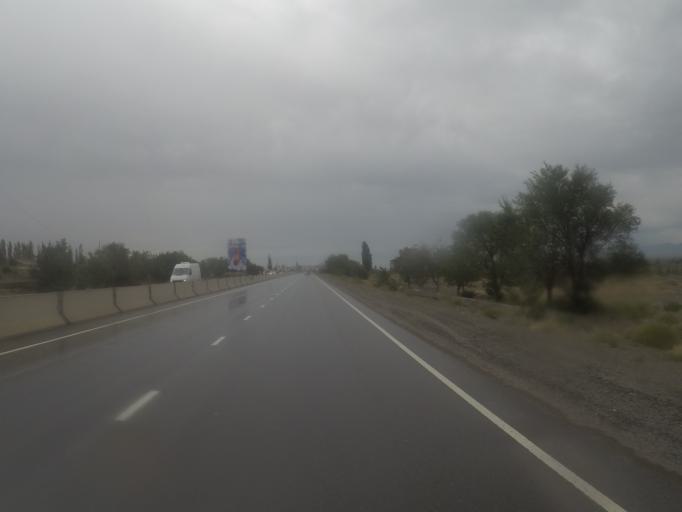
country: KG
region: Ysyk-Koel
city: Balykchy
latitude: 42.4563
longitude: 76.1407
